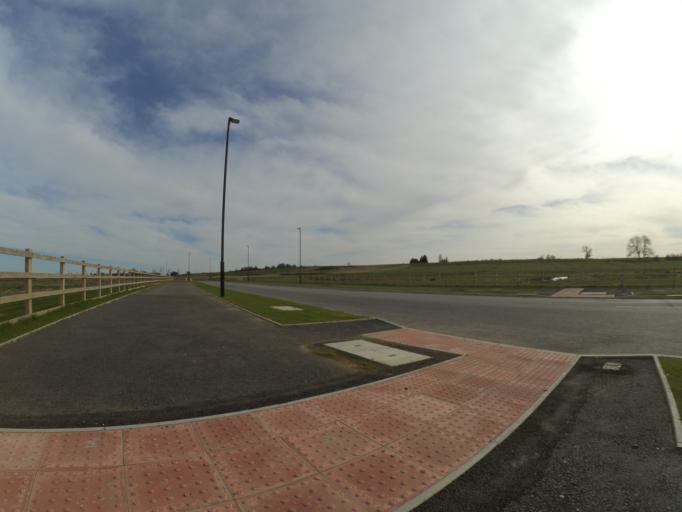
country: GB
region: England
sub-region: Warwickshire
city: Rugby
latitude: 52.3667
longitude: -1.2033
